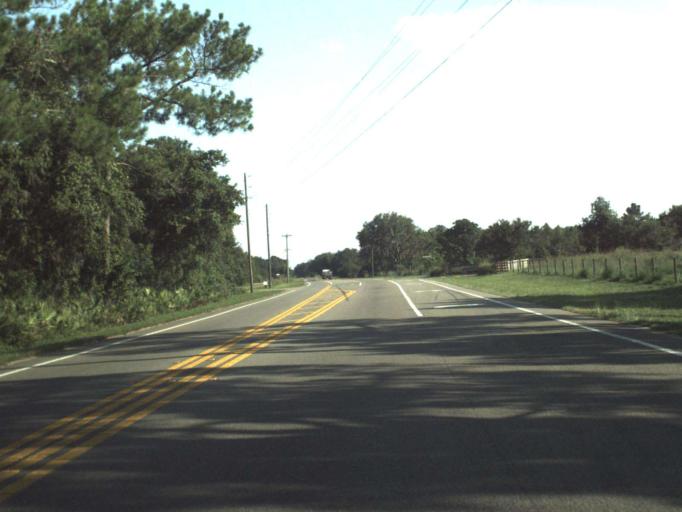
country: US
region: Florida
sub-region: Lake County
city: Groveland
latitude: 28.4397
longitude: -81.8335
